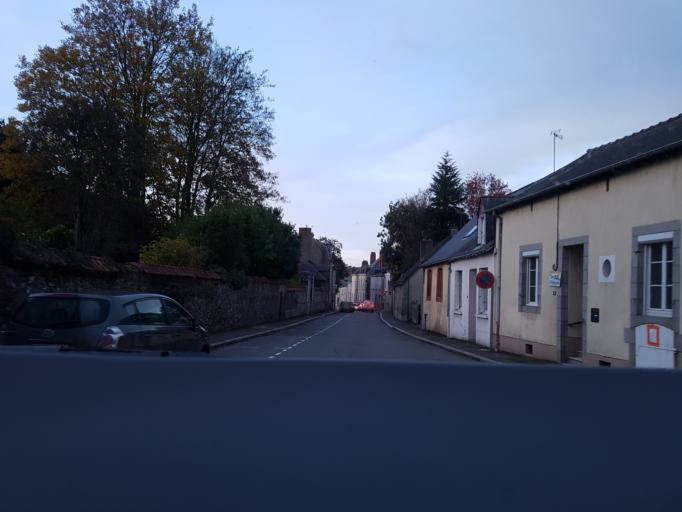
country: FR
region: Pays de la Loire
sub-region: Departement de la Mayenne
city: Cosse-le-Vivien
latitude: 47.9451
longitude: -0.9103
